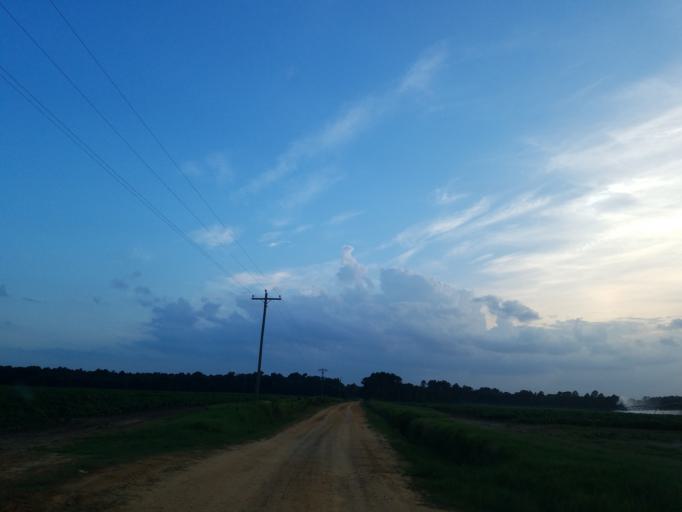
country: US
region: Georgia
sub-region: Dooly County
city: Vienna
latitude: 32.1489
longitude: -83.7277
